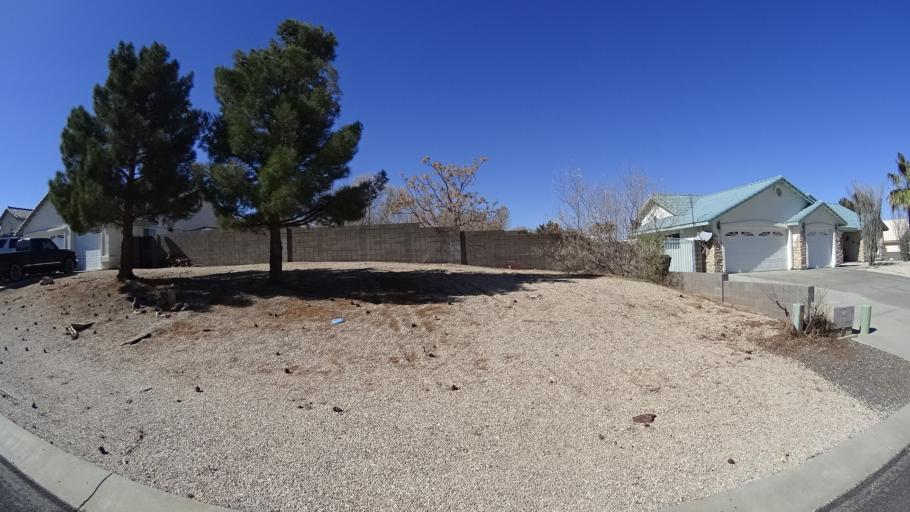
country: US
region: Arizona
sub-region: Mohave County
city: Kingman
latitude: 35.2015
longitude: -113.9621
